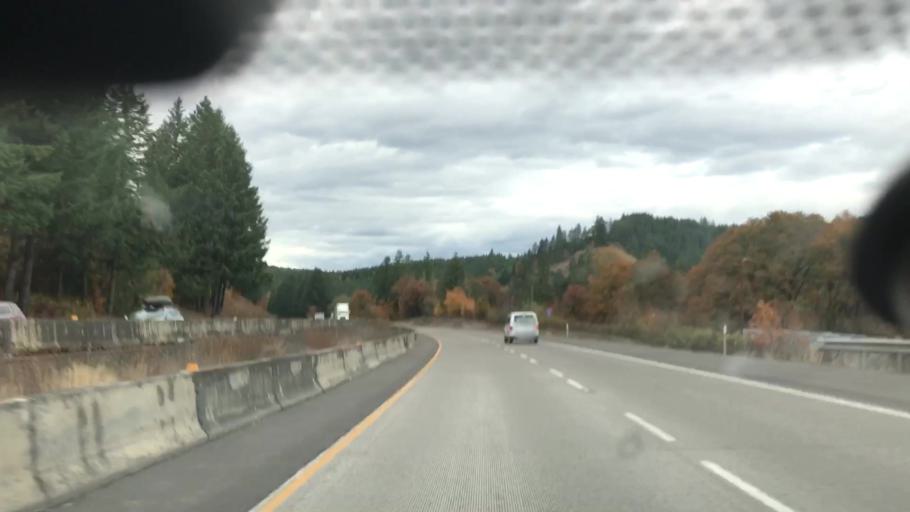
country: US
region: Oregon
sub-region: Douglas County
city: Yoncalla
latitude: 43.6165
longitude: -123.2146
